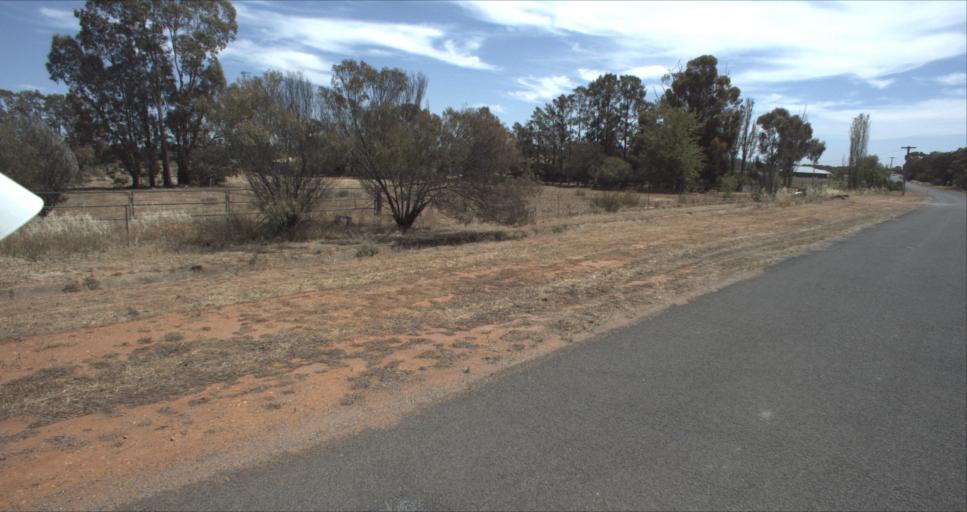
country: AU
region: New South Wales
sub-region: Leeton
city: Leeton
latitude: -34.5909
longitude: 146.4286
